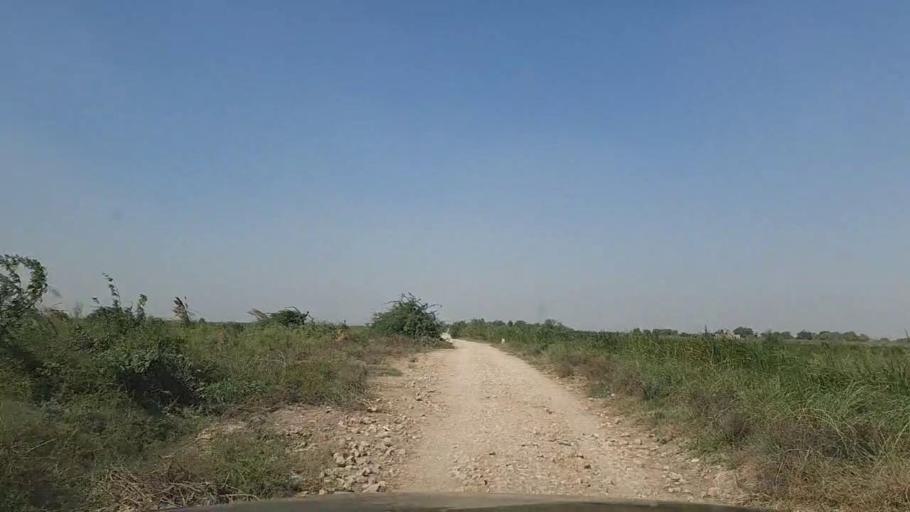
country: PK
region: Sindh
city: Daro Mehar
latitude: 24.8144
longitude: 68.1529
